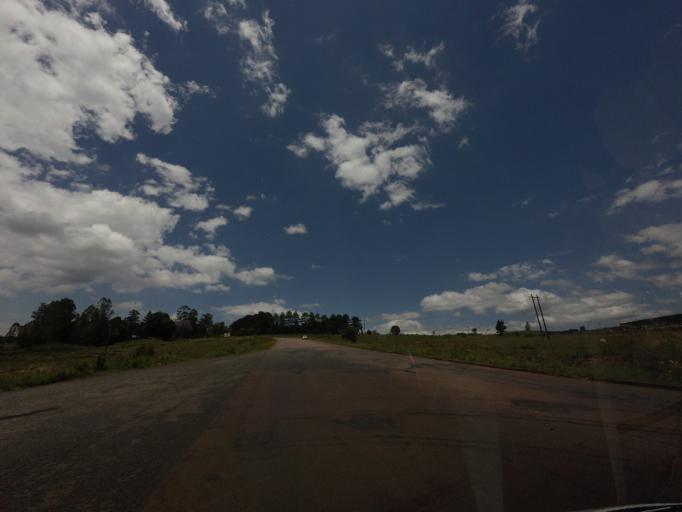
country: ZA
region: Mpumalanga
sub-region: Ehlanzeni District
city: Graksop
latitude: -25.0865
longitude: 30.7818
